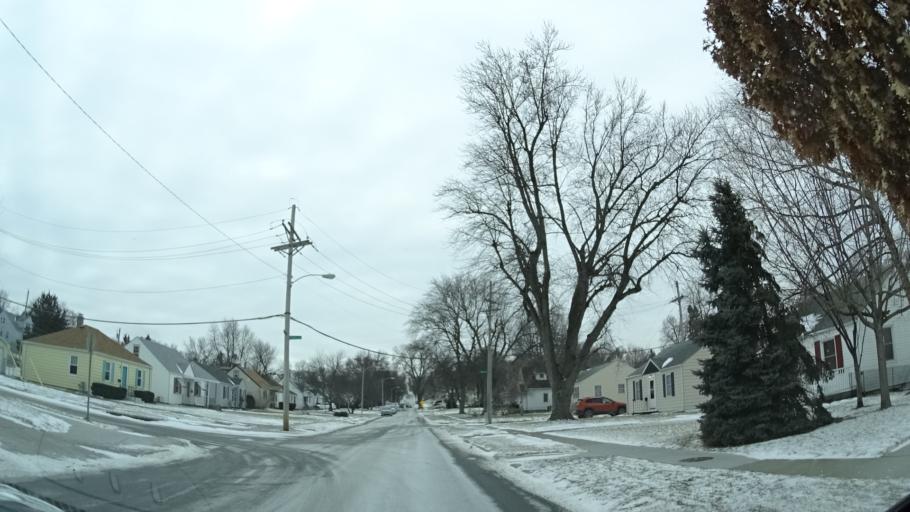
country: US
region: Nebraska
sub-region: Douglas County
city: Omaha
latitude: 41.2402
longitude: -95.9855
